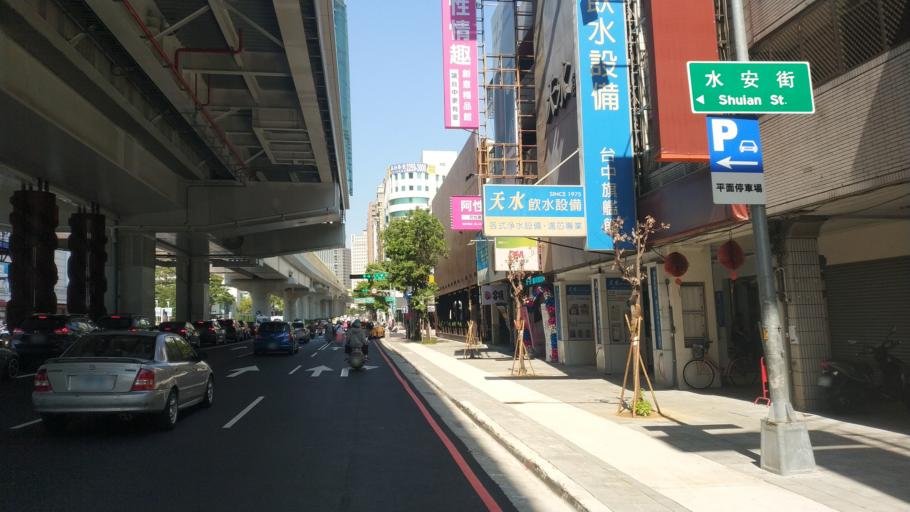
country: TW
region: Taiwan
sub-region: Taichung City
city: Taichung
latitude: 24.1530
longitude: 120.6469
